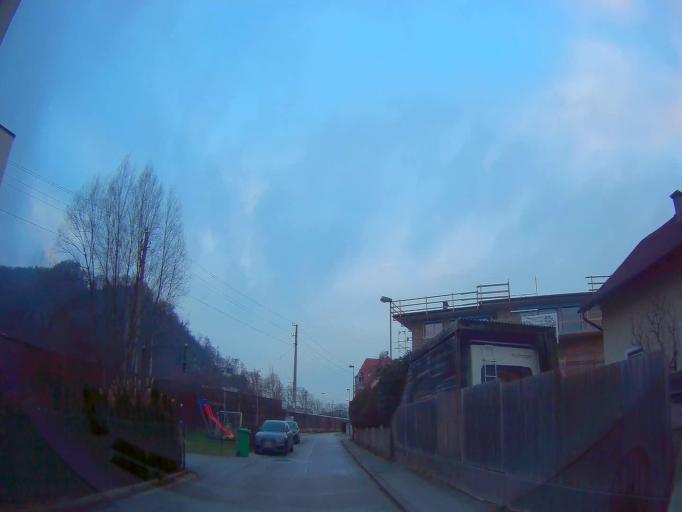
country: AT
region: Salzburg
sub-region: Salzburg Stadt
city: Salzburg
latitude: 47.8045
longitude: 13.0710
